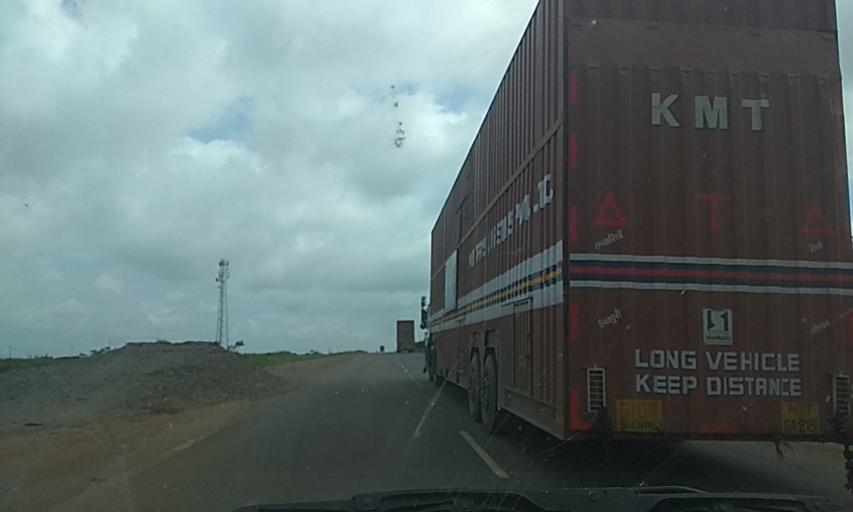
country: IN
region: Karnataka
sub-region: Dharwad
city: Hubli
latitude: 15.2668
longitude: 75.1453
